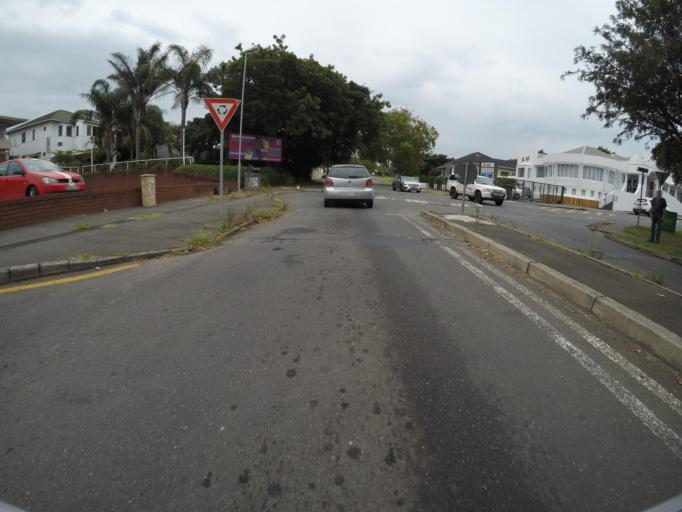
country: ZA
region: Eastern Cape
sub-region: Buffalo City Metropolitan Municipality
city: East London
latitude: -32.9822
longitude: 27.9022
